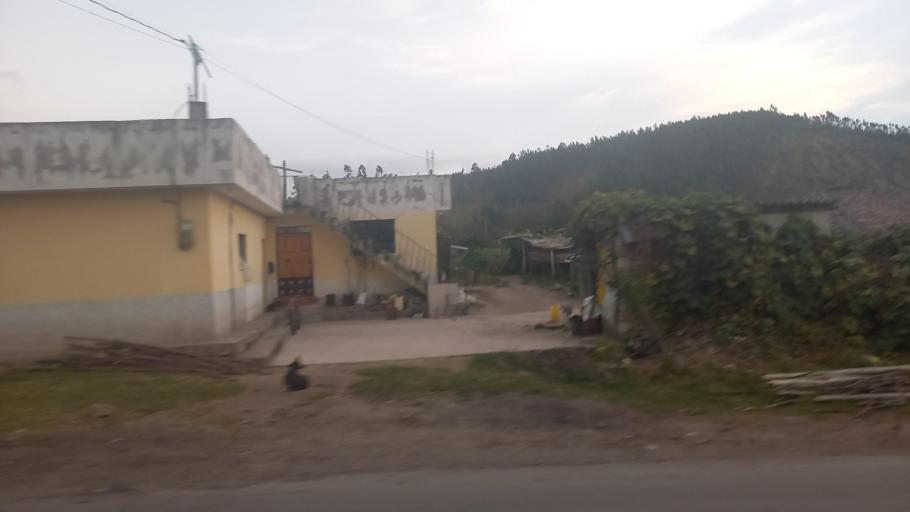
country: EC
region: Pichincha
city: Cayambe
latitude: 0.0702
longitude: -78.1133
